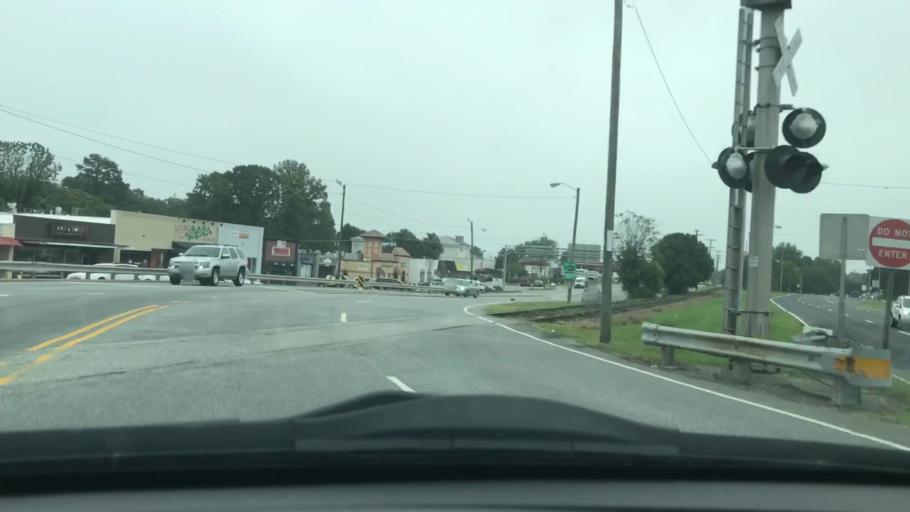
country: US
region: North Carolina
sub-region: Guilford County
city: Greensboro
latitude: 36.0962
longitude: -79.8174
